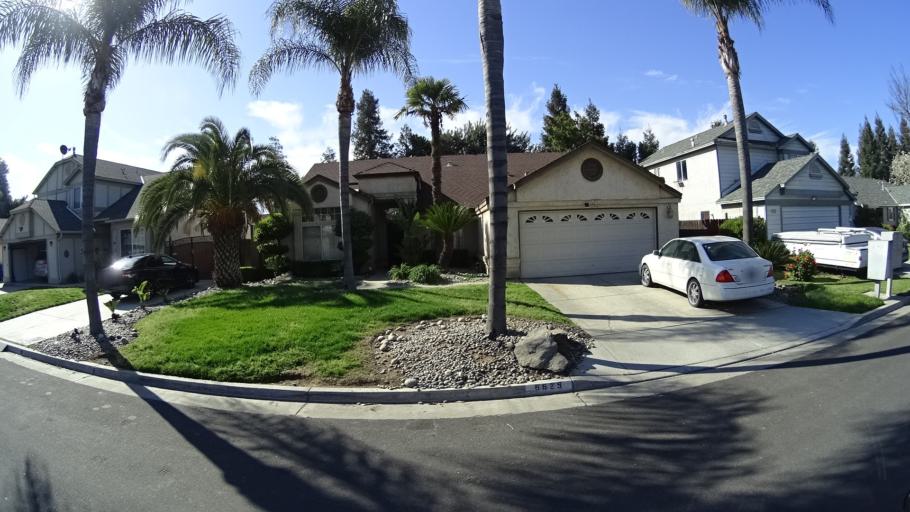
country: US
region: California
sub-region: Fresno County
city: West Park
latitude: 36.7968
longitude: -119.8922
